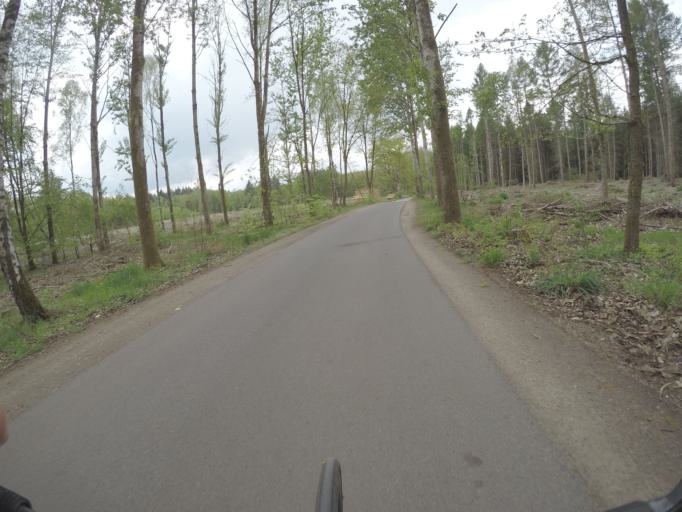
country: DE
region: Brandenburg
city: Marienwerder
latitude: 52.8984
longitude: 13.6592
